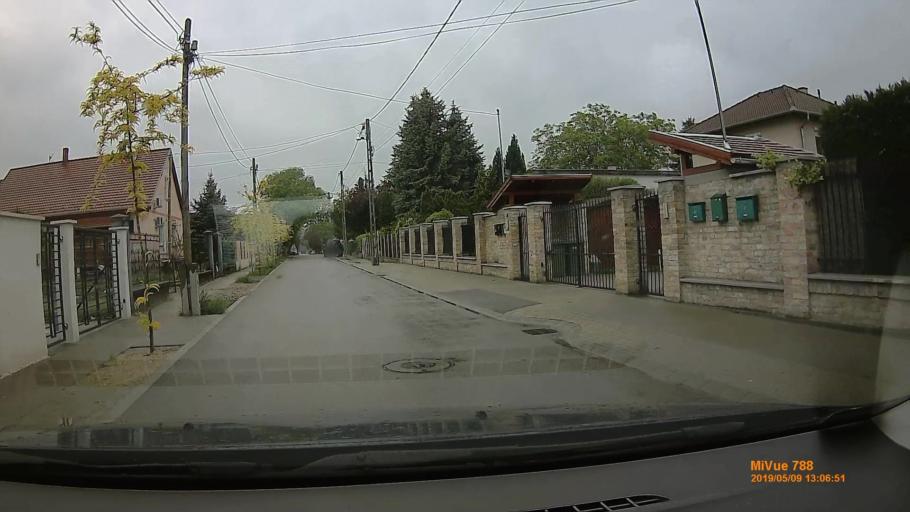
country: HU
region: Budapest
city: Budapest XVI. keruelet
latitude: 47.5341
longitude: 19.1769
